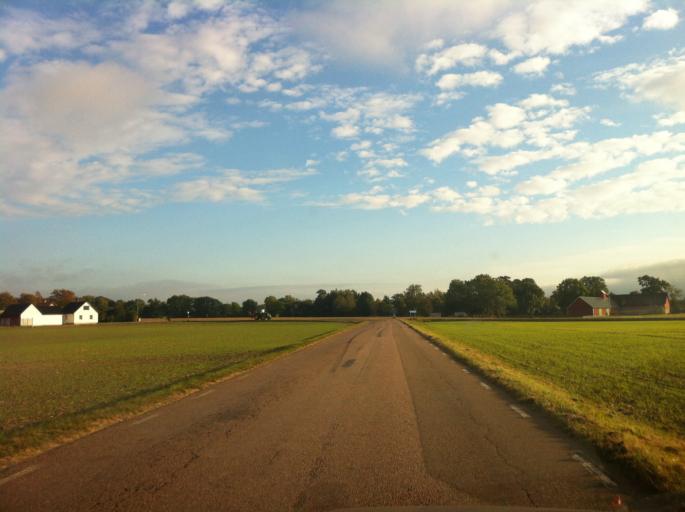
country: SE
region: Skane
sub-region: Helsingborg
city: Barslov
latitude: 55.9946
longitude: 12.8229
